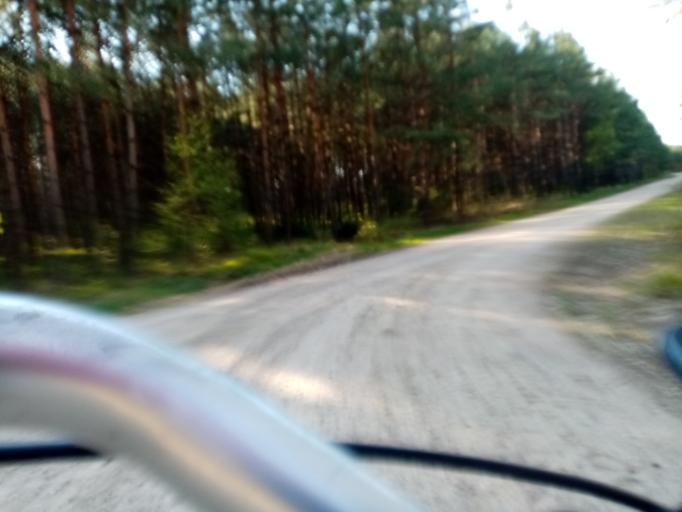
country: PL
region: Kujawsko-Pomorskie
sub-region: Powiat brodnicki
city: Gorzno
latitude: 53.1550
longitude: 19.7014
